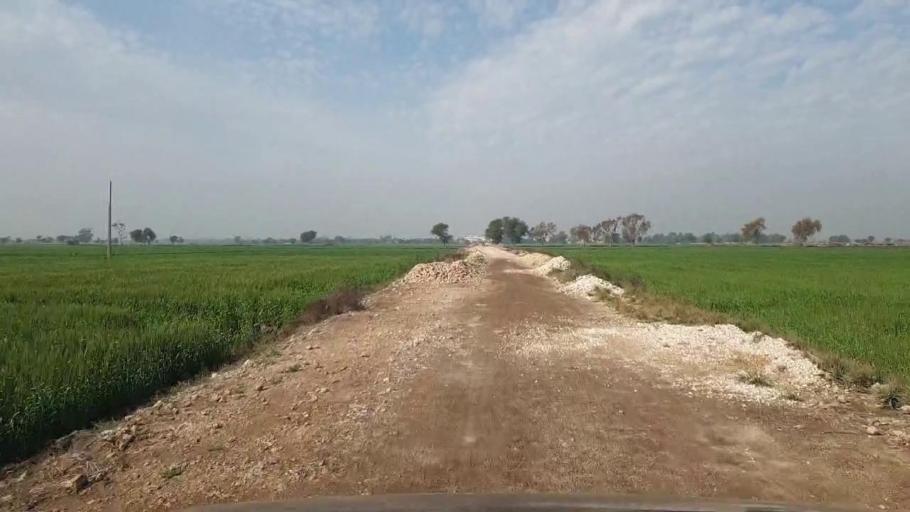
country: PK
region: Sindh
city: Hala
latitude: 25.9917
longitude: 68.3842
